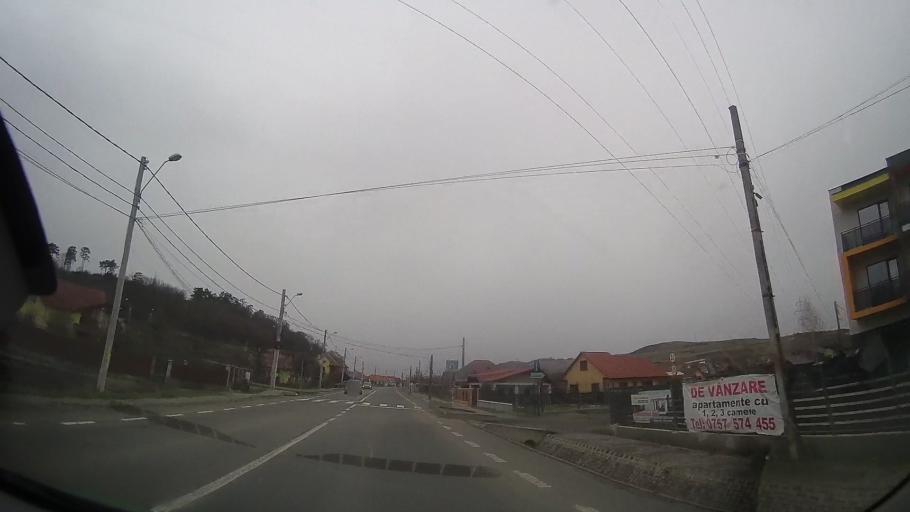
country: RO
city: Remetea
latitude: 46.5957
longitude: 24.5321
